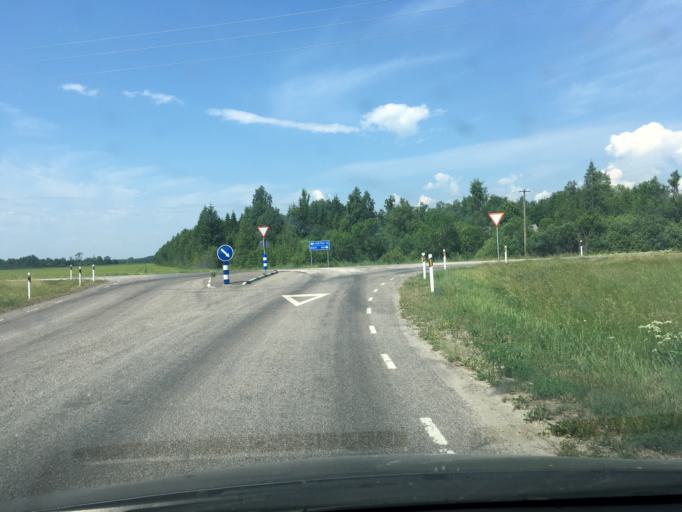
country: EE
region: Laeaene
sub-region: Lihula vald
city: Lihula
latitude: 58.6687
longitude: 23.7663
